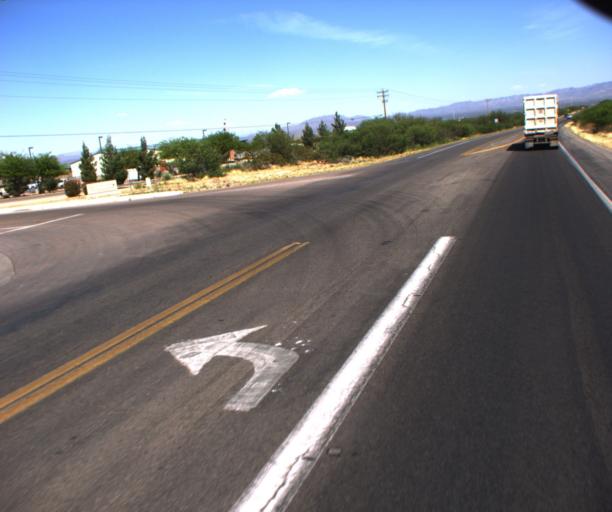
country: US
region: Arizona
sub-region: Cochise County
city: Sierra Vista
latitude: 31.5545
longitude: -110.2070
